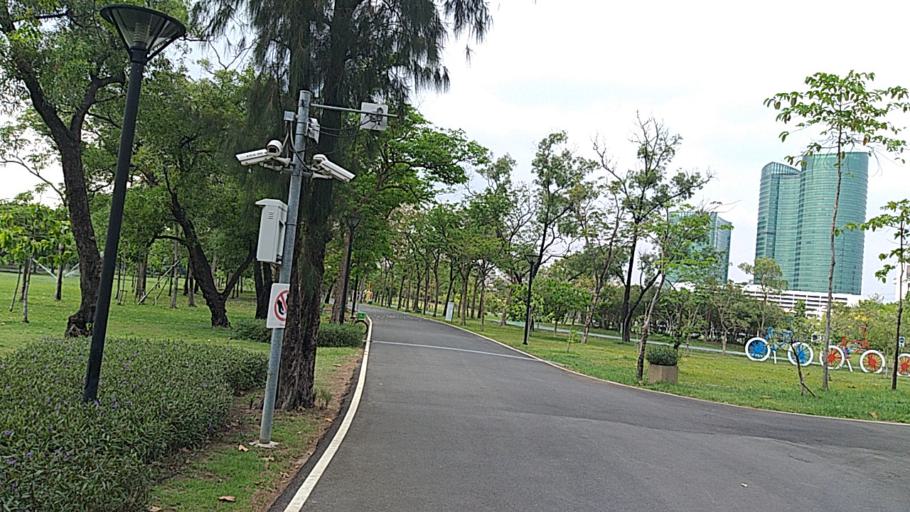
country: TH
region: Bangkok
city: Chatuchak
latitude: 13.8138
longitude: 100.5551
